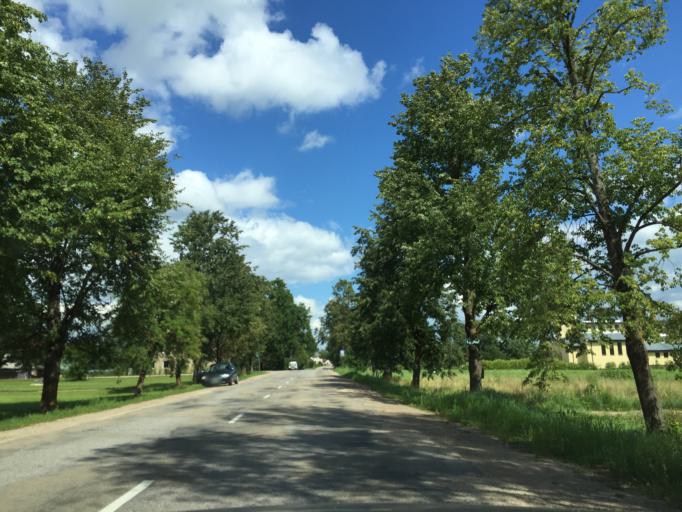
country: LV
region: Malpils
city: Malpils
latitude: 56.9023
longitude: 24.9242
